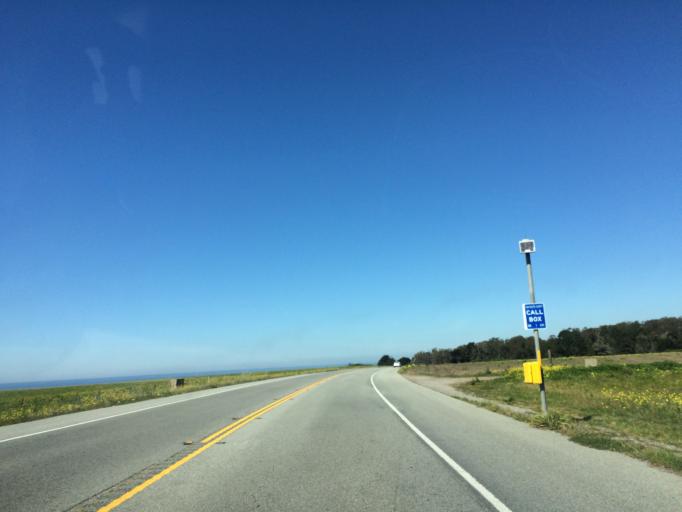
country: US
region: California
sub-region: San Mateo County
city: Half Moon Bay
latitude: 37.3978
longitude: -122.4168
